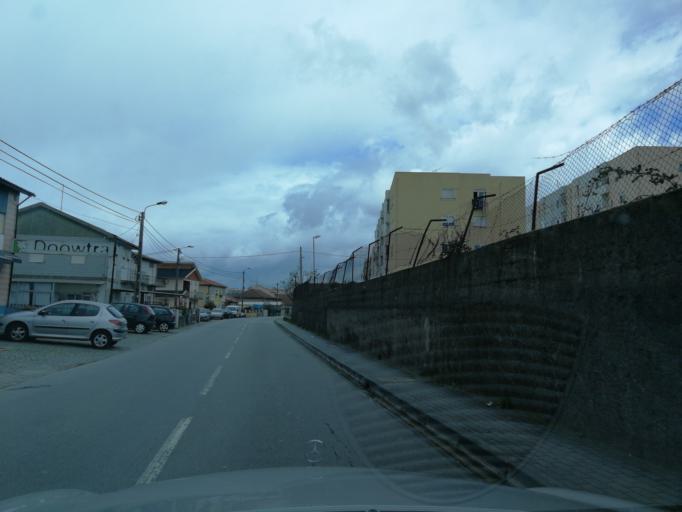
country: PT
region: Braga
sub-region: Braga
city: Braga
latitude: 41.5368
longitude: -8.4293
